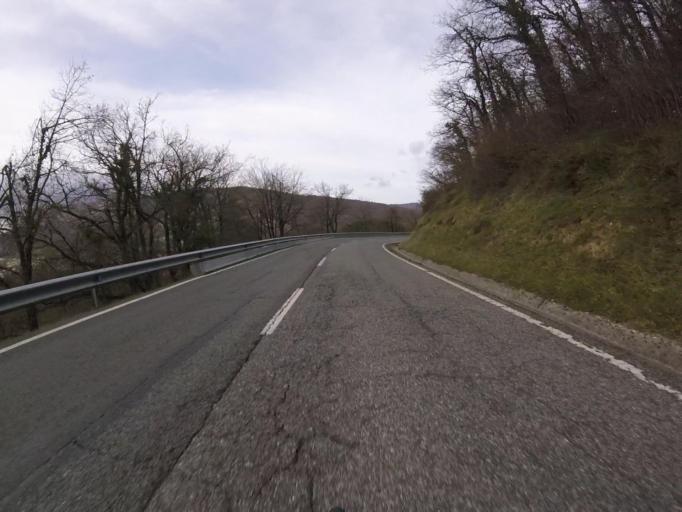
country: ES
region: Navarre
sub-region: Provincia de Navarra
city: Olazagutia
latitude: 42.8736
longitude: -2.1832
